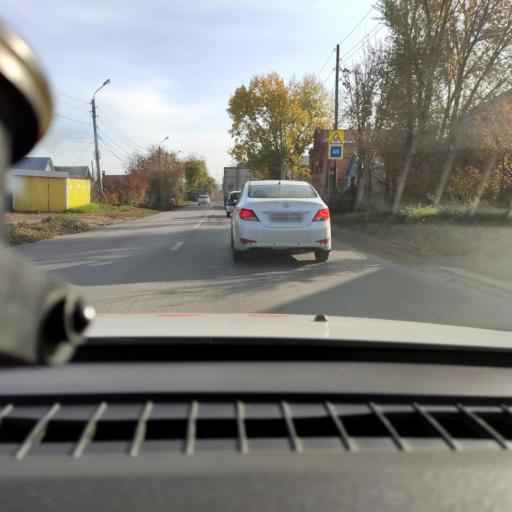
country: RU
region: Samara
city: Samara
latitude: 53.1769
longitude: 50.1697
